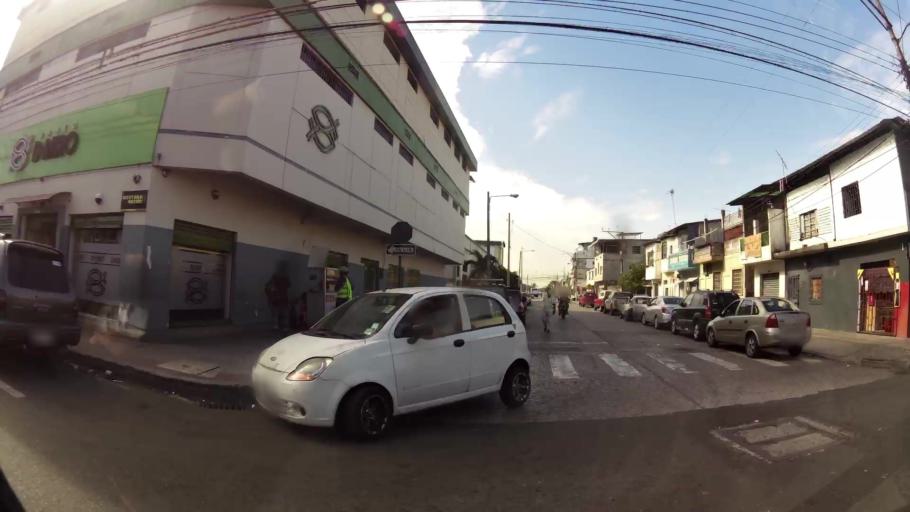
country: EC
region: Guayas
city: Guayaquil
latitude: -2.2013
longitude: -79.9171
